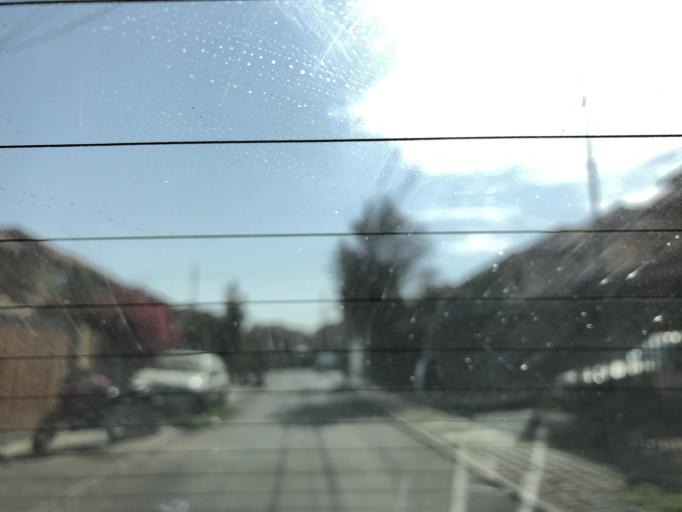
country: CL
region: Santiago Metropolitan
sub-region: Provincia de Cordillera
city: Puente Alto
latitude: -33.5769
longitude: -70.5427
